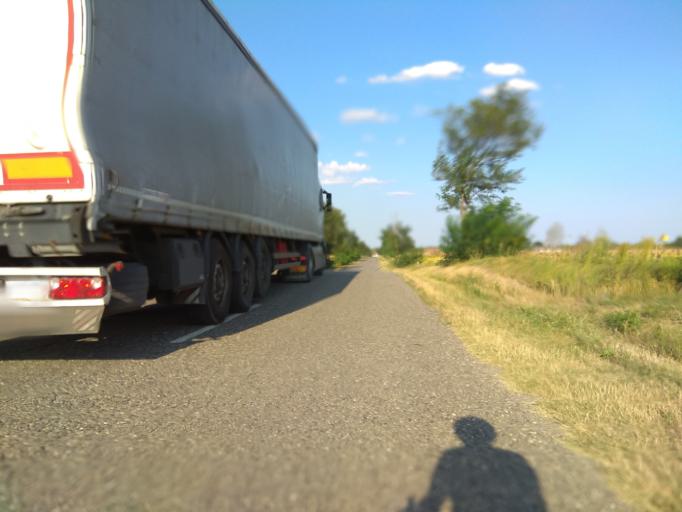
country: HU
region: Borsod-Abauj-Zemplen
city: Onod
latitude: 47.9789
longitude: 20.9154
